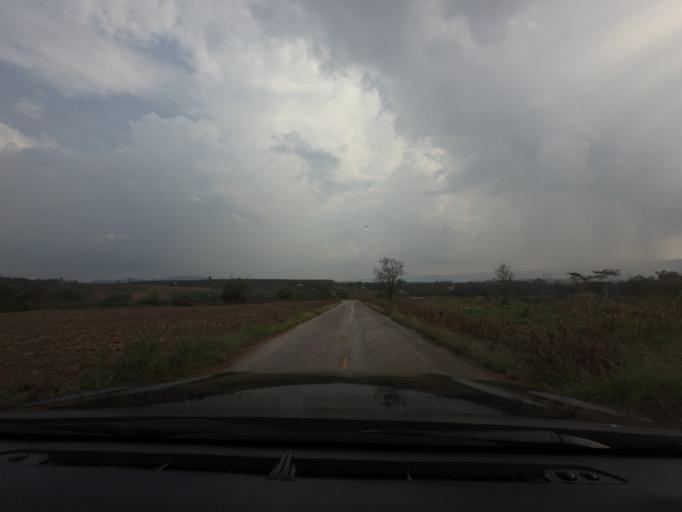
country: TH
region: Nakhon Ratchasima
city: Wang Nam Khiao
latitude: 14.4201
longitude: 101.7356
